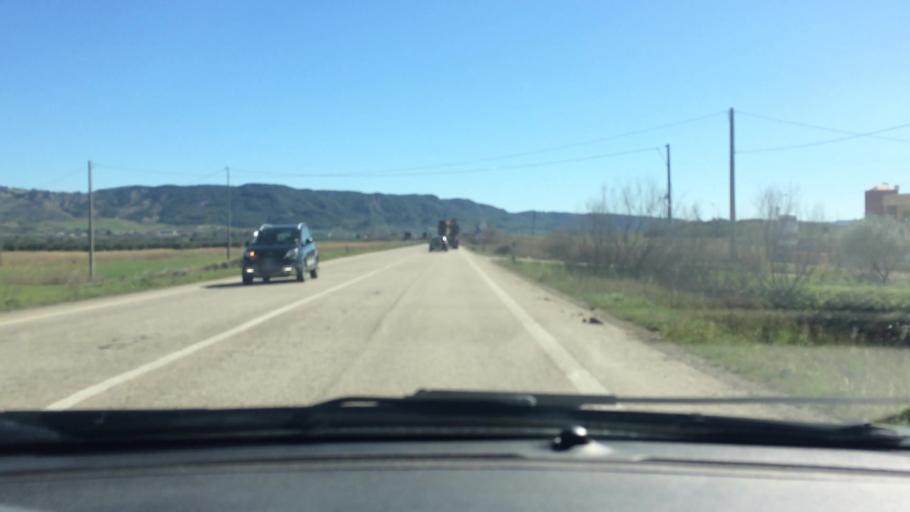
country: IT
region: Basilicate
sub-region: Provincia di Matera
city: Montescaglioso
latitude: 40.5317
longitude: 16.6135
